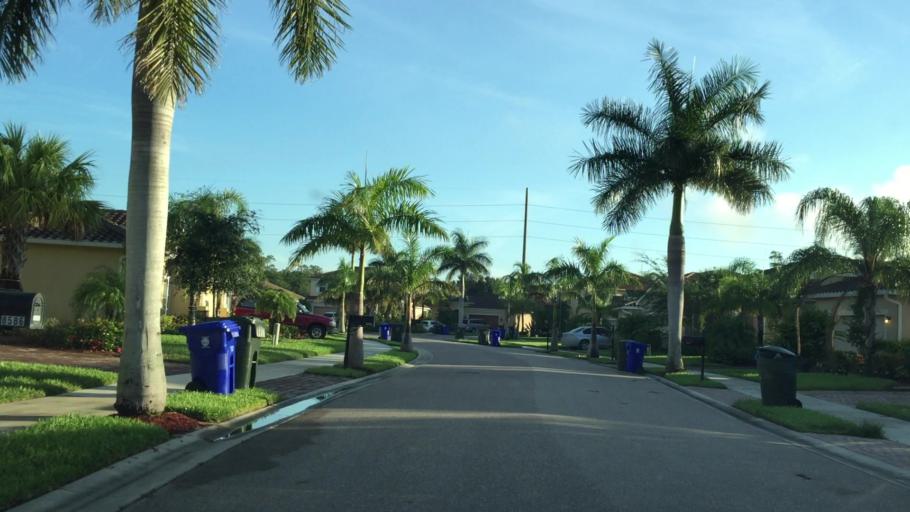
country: US
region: Florida
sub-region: Lee County
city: Gateway
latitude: 26.6255
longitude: -81.7642
